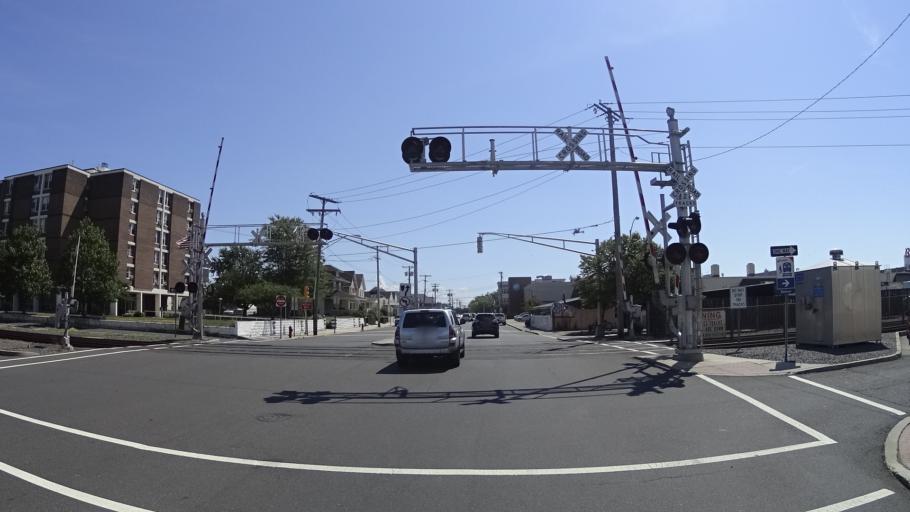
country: US
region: New Jersey
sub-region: Monmouth County
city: Belmar
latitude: 40.1819
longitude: -74.0272
